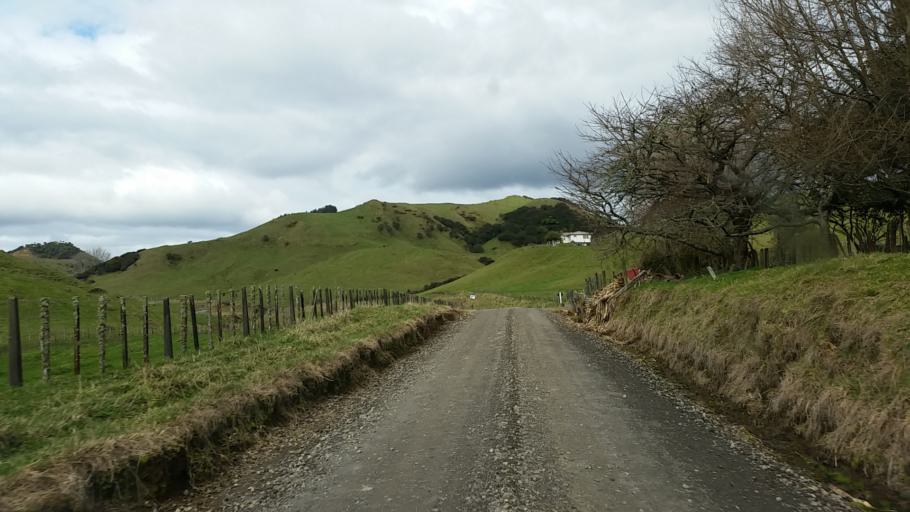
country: NZ
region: Taranaki
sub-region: New Plymouth District
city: Waitara
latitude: -39.1672
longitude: 174.6021
